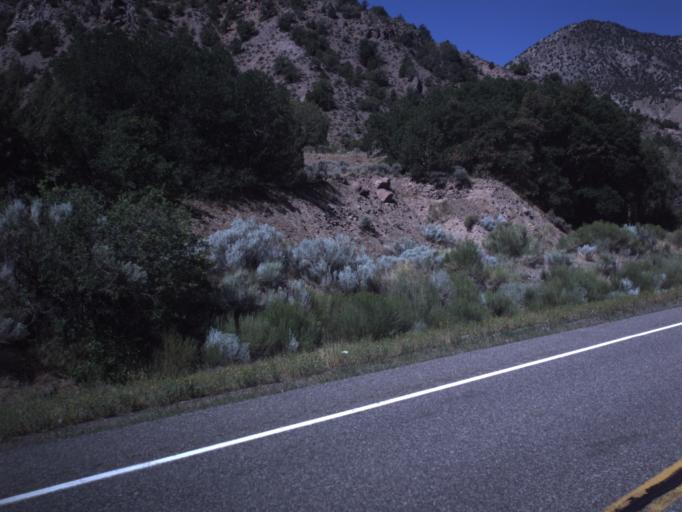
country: US
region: Utah
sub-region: Sevier County
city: Monroe
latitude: 38.5675
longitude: -112.2567
